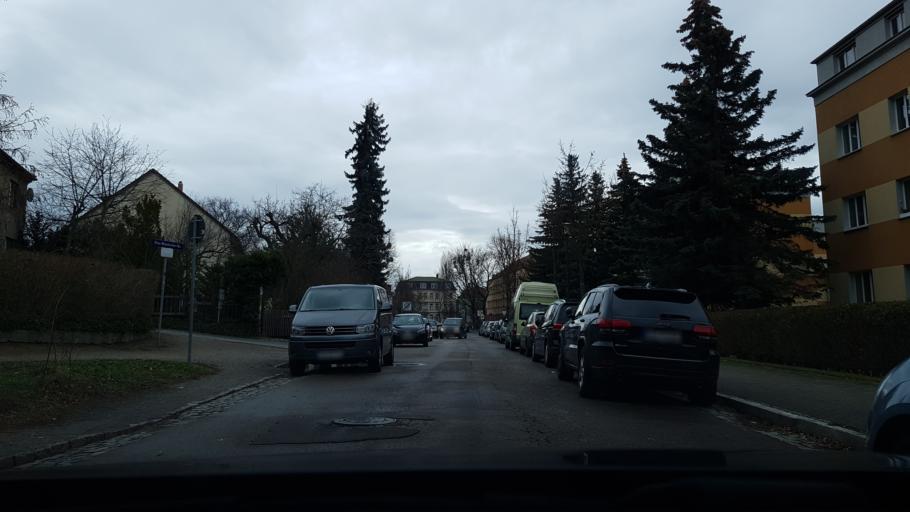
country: DE
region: Saxony
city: Dresden
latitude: 51.0236
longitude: 13.7663
